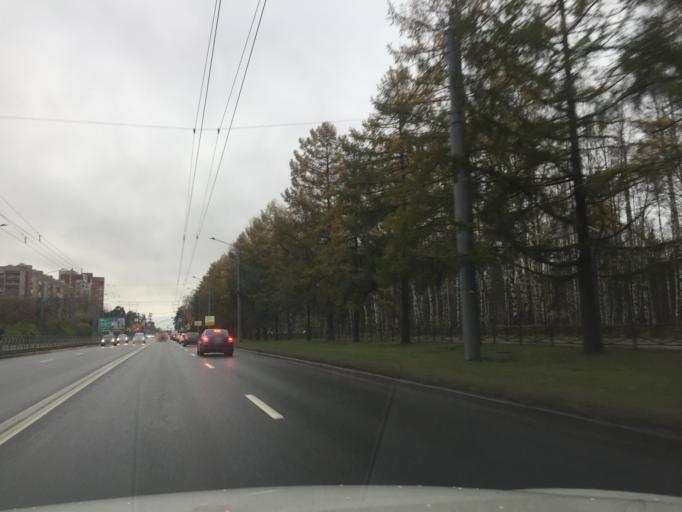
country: RU
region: St.-Petersburg
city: Sosnovka
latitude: 60.0146
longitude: 30.3568
